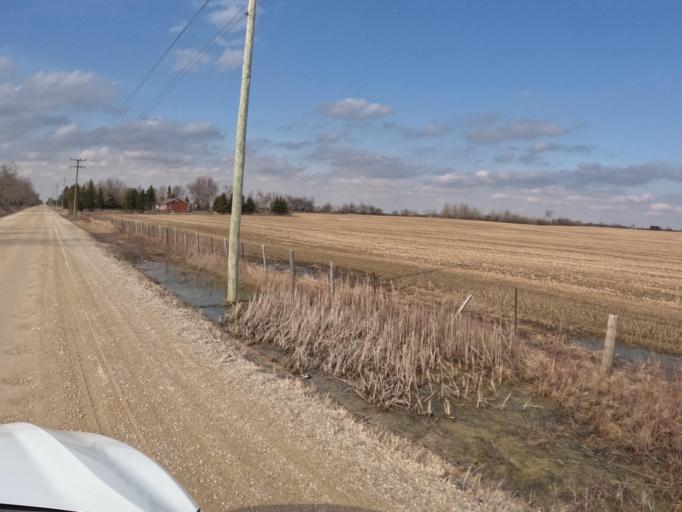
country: CA
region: Ontario
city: Shelburne
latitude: 43.9085
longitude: -80.3032
